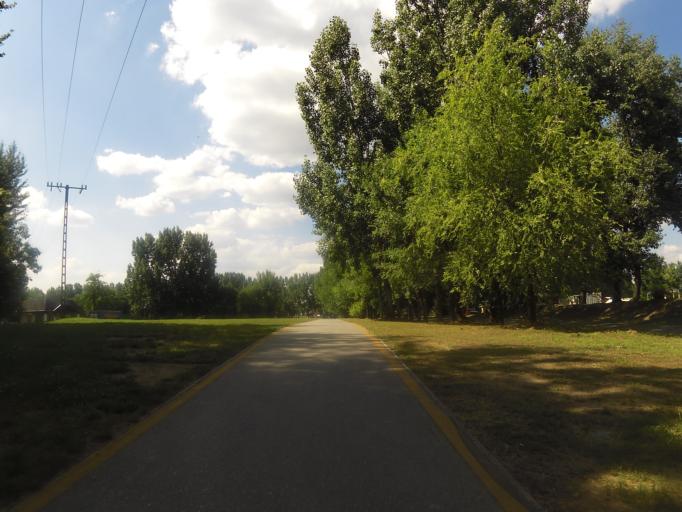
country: HU
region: Jasz-Nagykun-Szolnok
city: Tiszafured
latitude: 47.6226
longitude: 20.7377
